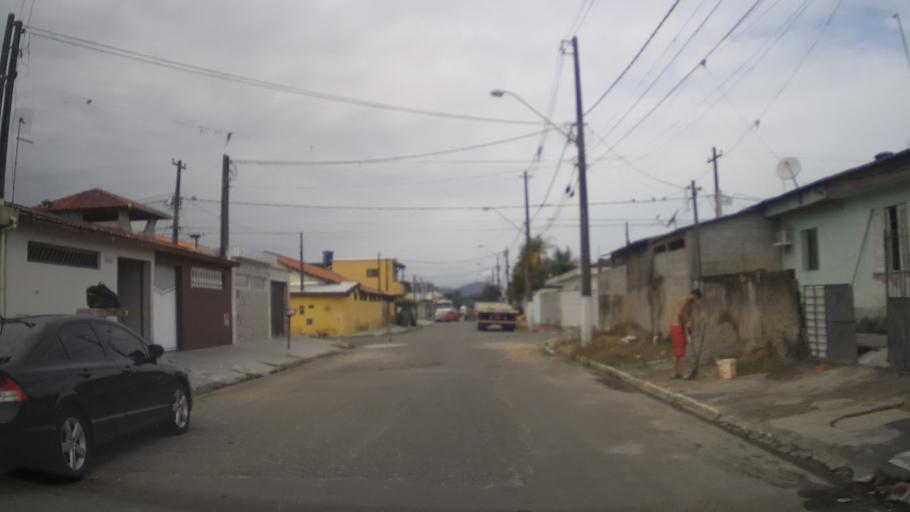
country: BR
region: Sao Paulo
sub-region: Praia Grande
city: Praia Grande
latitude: -24.0053
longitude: -46.4501
